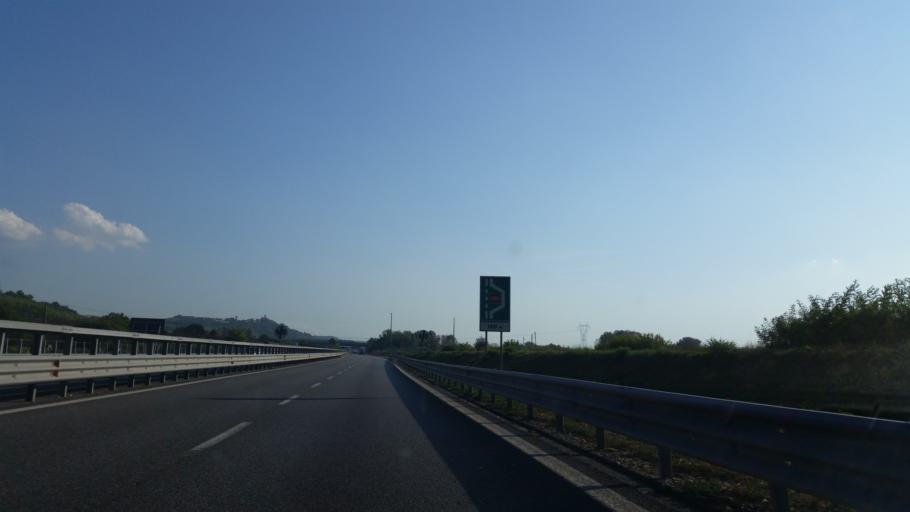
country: IT
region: Piedmont
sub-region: Provincia di Asti
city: Mongardino
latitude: 44.8612
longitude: 8.2034
